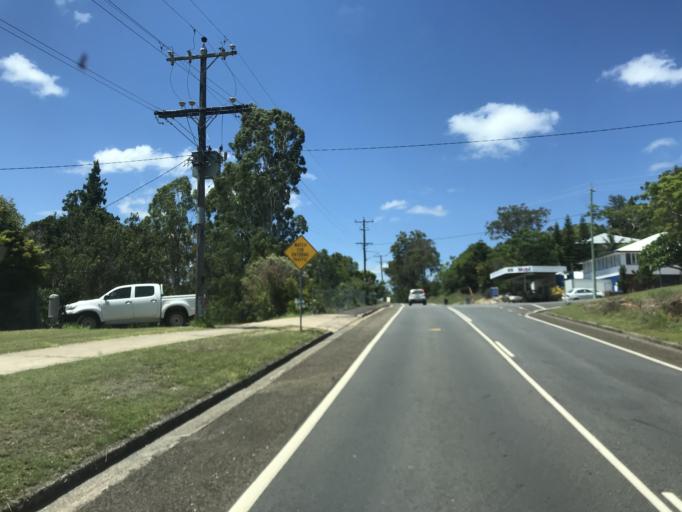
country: AU
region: Queensland
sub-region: Tablelands
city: Atherton
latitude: -17.3871
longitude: 145.3870
